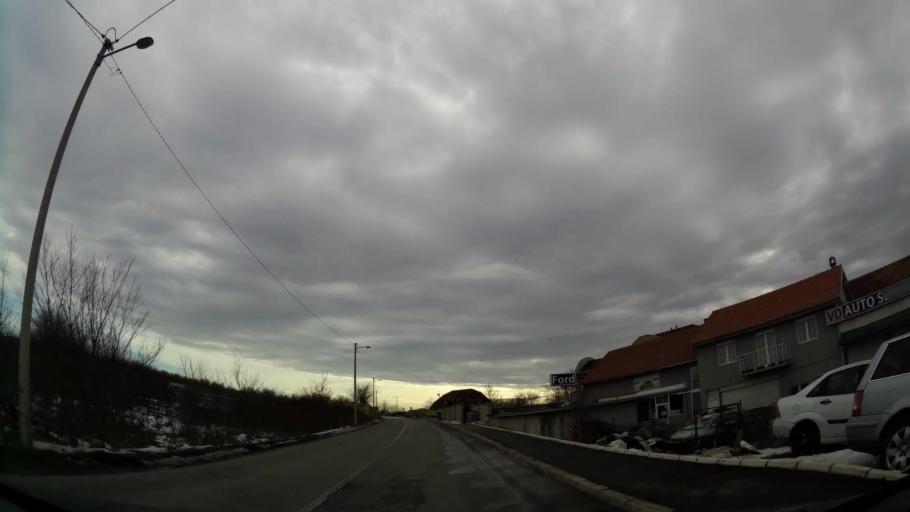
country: RS
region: Central Serbia
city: Sremcica
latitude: 44.7278
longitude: 20.3888
